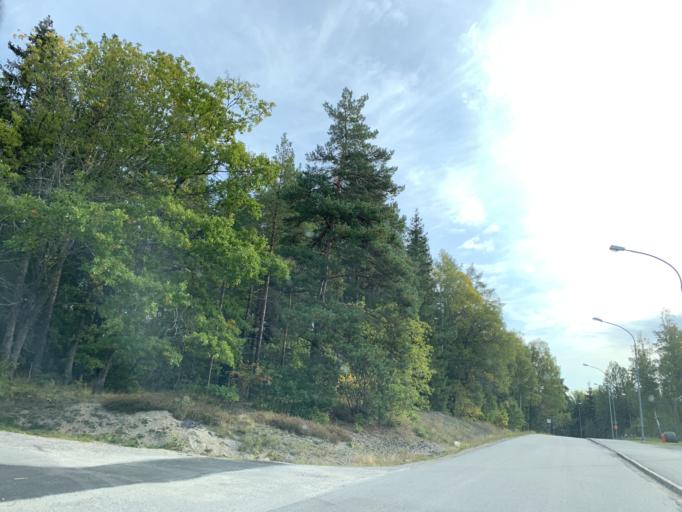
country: SE
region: Soedermanland
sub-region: Eskilstuna Kommun
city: Eskilstuna
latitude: 59.3622
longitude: 16.5457
